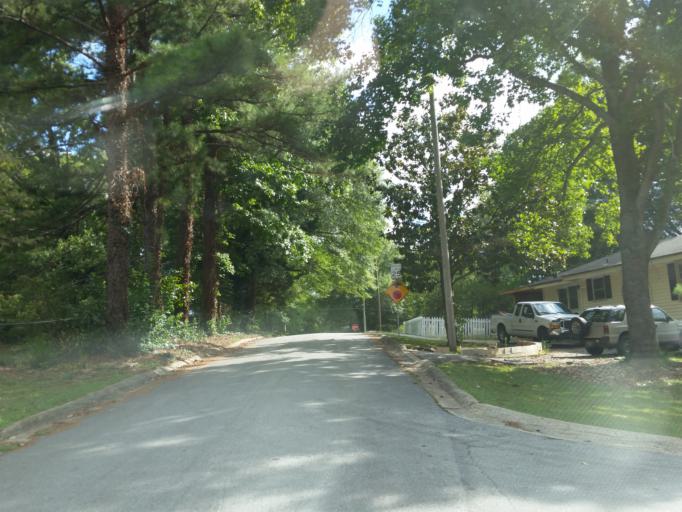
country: US
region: Georgia
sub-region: Cobb County
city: Smyrna
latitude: 33.8780
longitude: -84.5247
